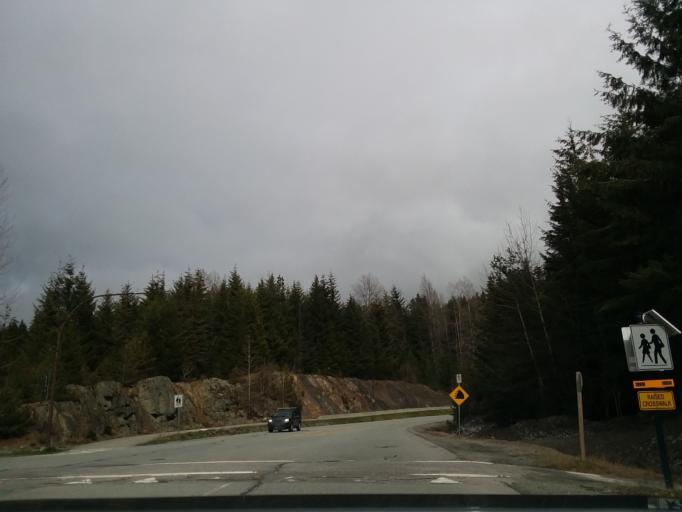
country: CA
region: British Columbia
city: Whistler
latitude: 50.1273
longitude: -122.9646
